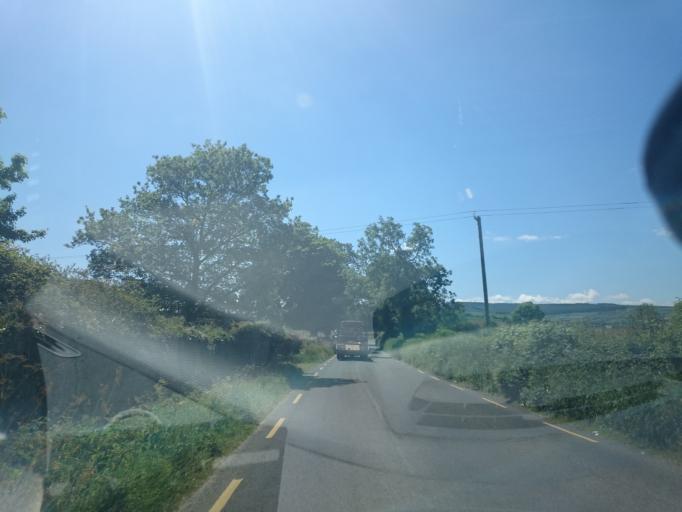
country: IE
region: Leinster
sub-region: Kilkenny
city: Graiguenamanagh
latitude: 52.6033
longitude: -6.9916
